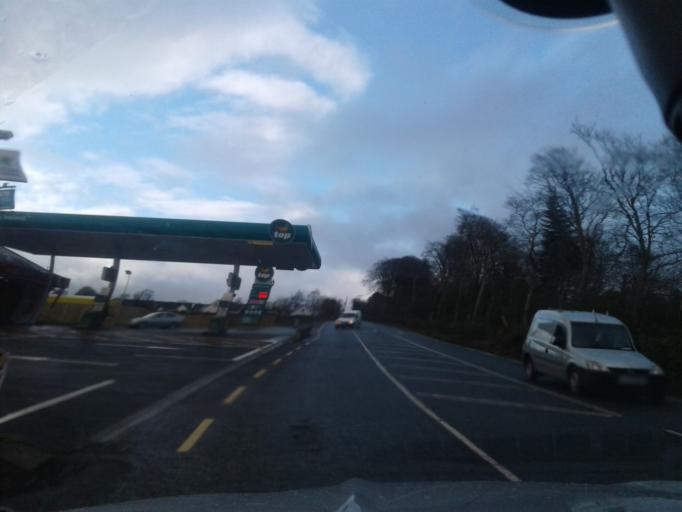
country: IE
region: Ulster
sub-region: County Donegal
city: Ramelton
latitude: 55.0202
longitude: -7.6524
